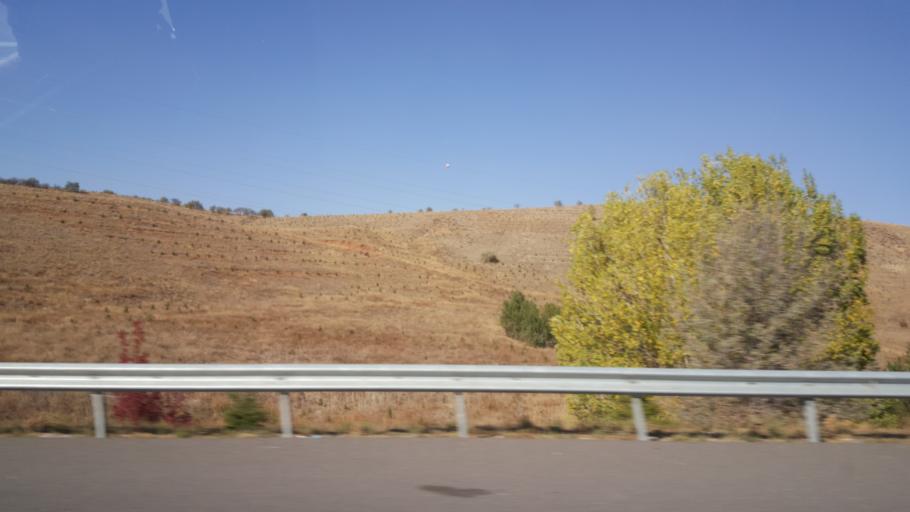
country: TR
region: Ankara
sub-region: Goelbasi
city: Golbasi
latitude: 39.8126
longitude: 32.8279
